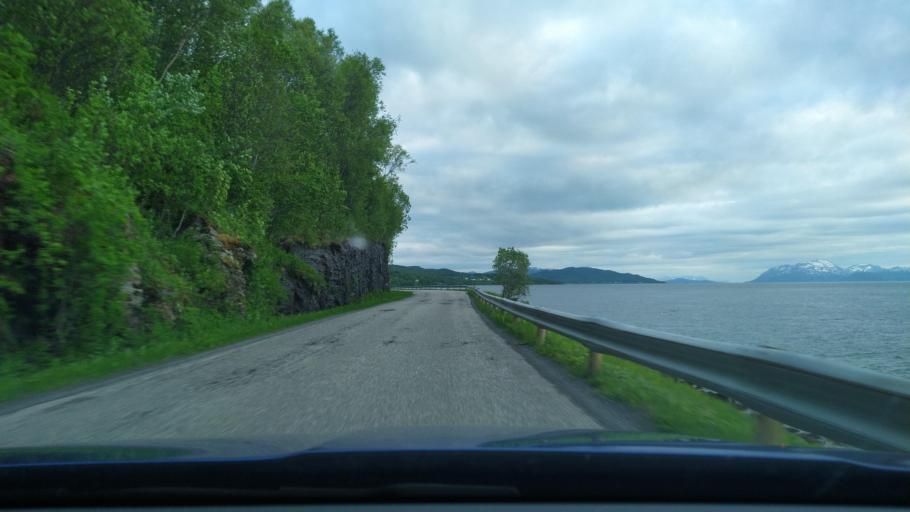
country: NO
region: Troms
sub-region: Lenvik
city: Finnsnes
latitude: 69.1426
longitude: 17.9179
